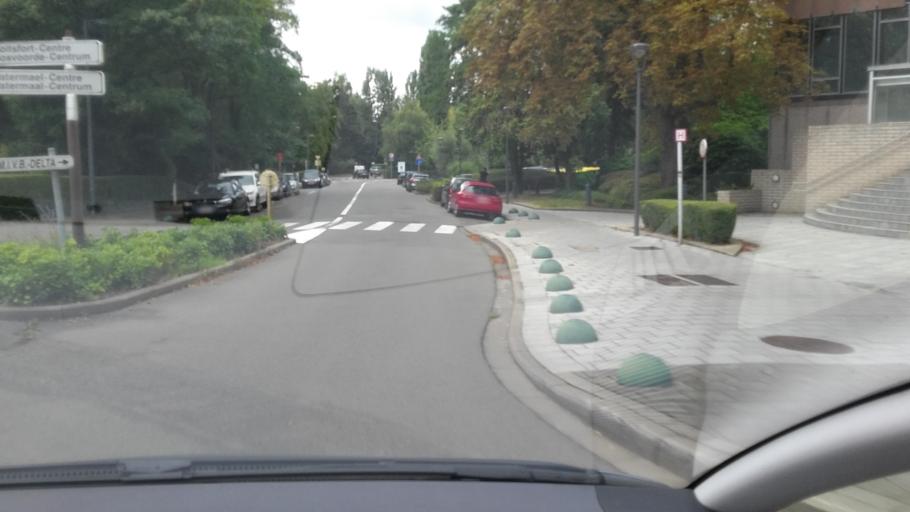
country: BE
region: Flanders
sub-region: Provincie Vlaams-Brabant
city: Hoeilaart
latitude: 50.8140
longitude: 4.4166
